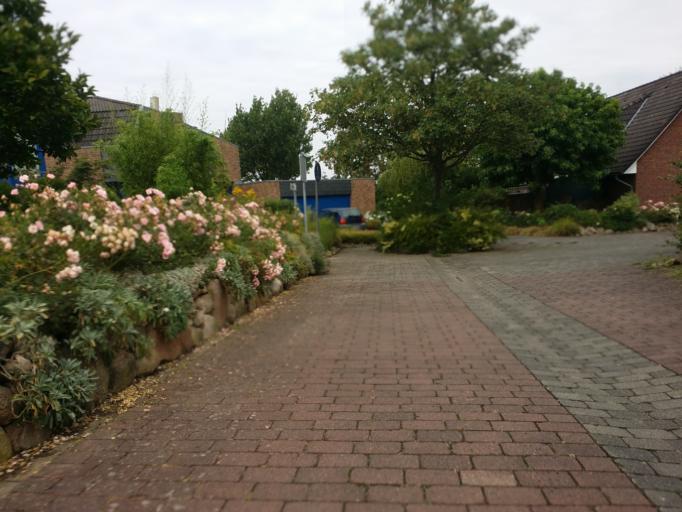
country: DE
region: Schleswig-Holstein
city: Oldendorf
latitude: 53.9510
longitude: 9.4577
